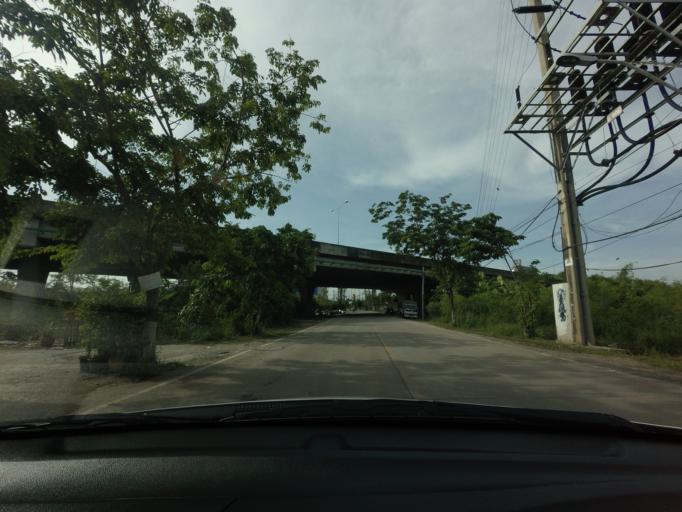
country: TH
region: Bangkok
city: Bang Na
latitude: 13.6229
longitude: 100.6663
